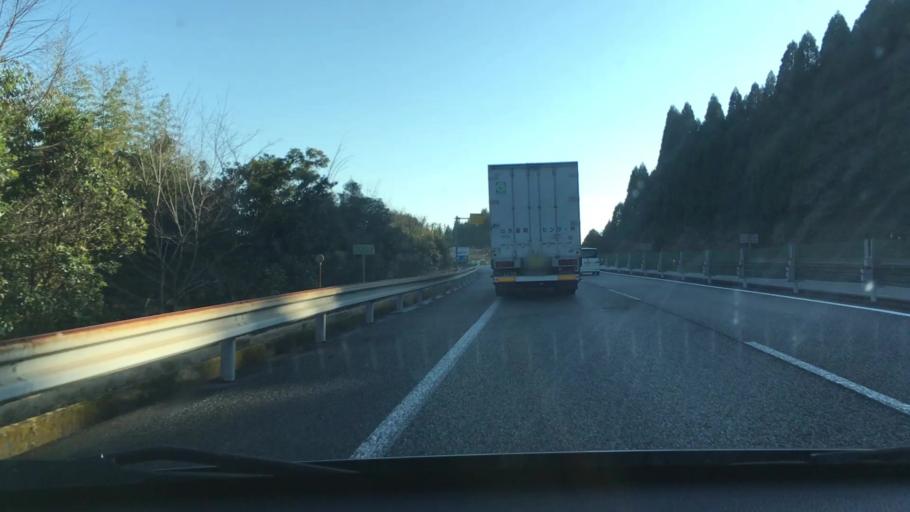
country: JP
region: Kagoshima
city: Kajiki
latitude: 31.8256
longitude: 130.6938
